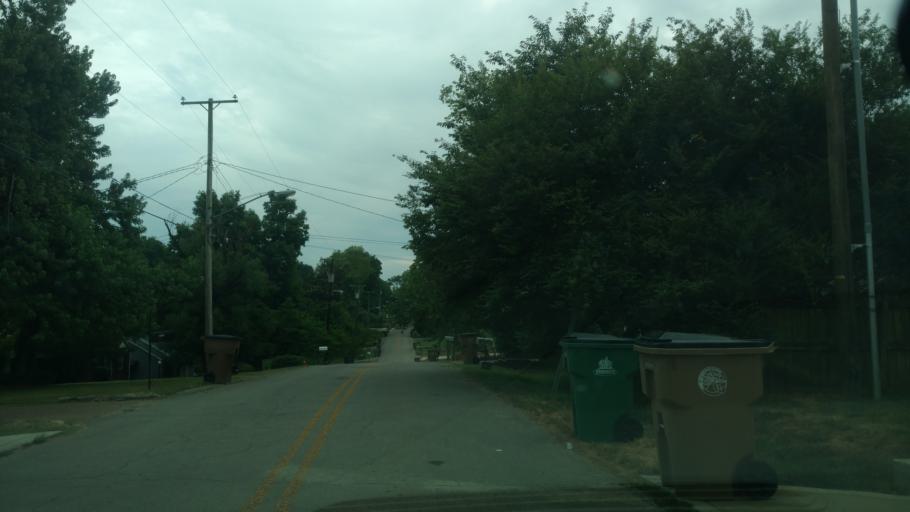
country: US
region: Tennessee
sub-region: Davidson County
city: Nashville
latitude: 36.1951
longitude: -86.7134
